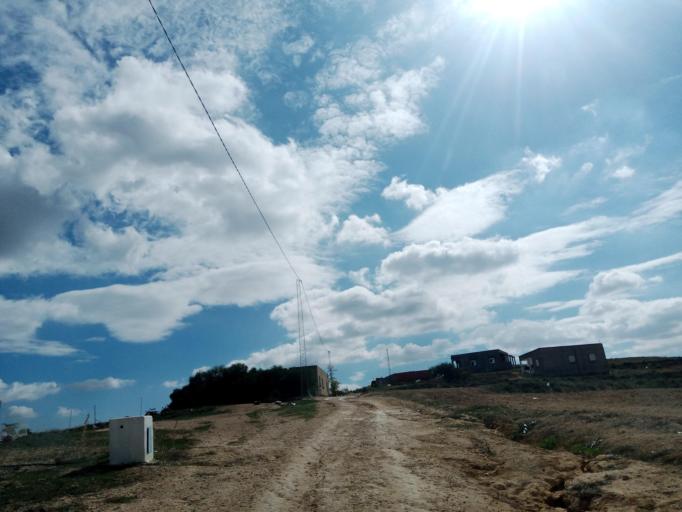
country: TN
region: Tunis
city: Oued Lill
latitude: 36.8102
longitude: 9.9821
